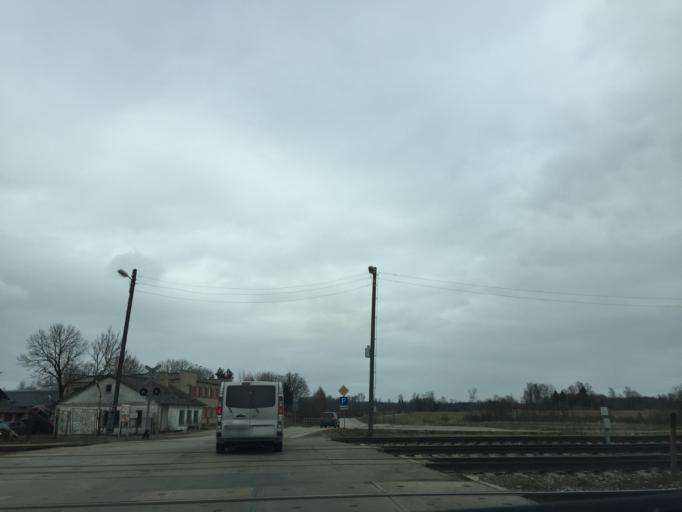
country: LV
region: Kraslavas Rajons
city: Kraslava
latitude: 55.9267
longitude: 27.1413
